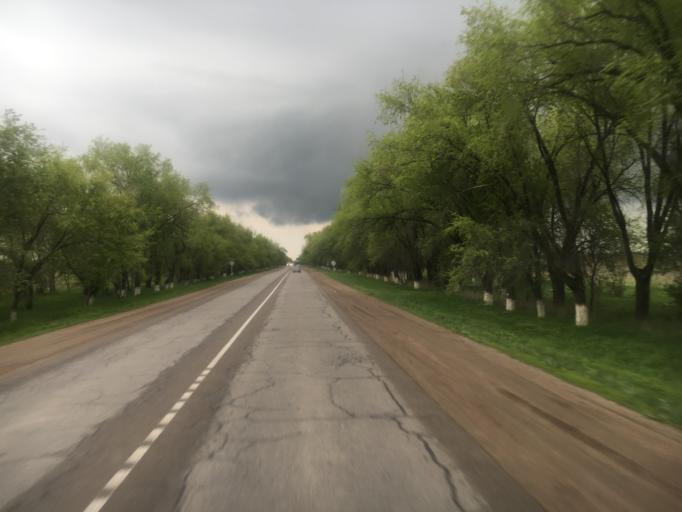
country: KZ
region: Almaty Oblysy
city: Burunday
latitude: 43.2531
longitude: 76.6682
